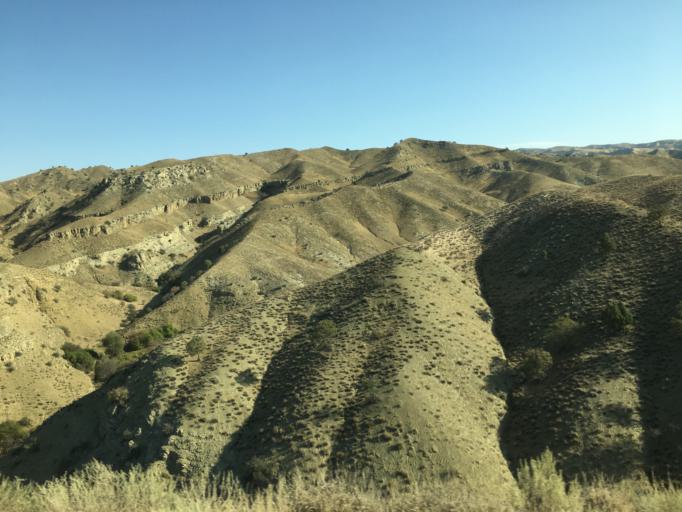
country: TM
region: Balkan
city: Magtymguly
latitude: 38.3035
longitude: 56.7985
